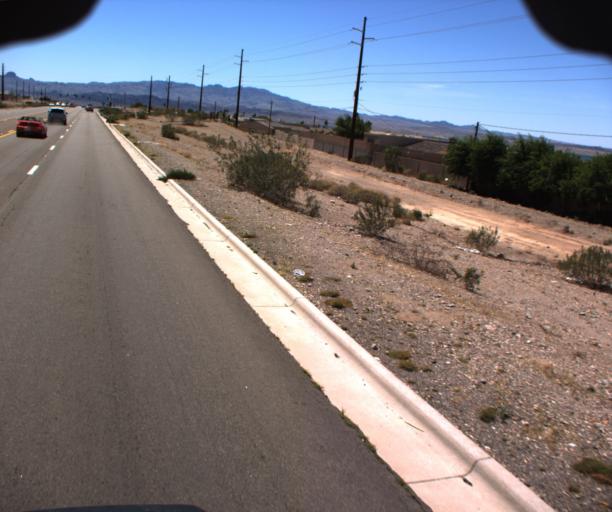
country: US
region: Arizona
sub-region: Mohave County
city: Desert Hills
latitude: 34.5205
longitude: -114.3496
